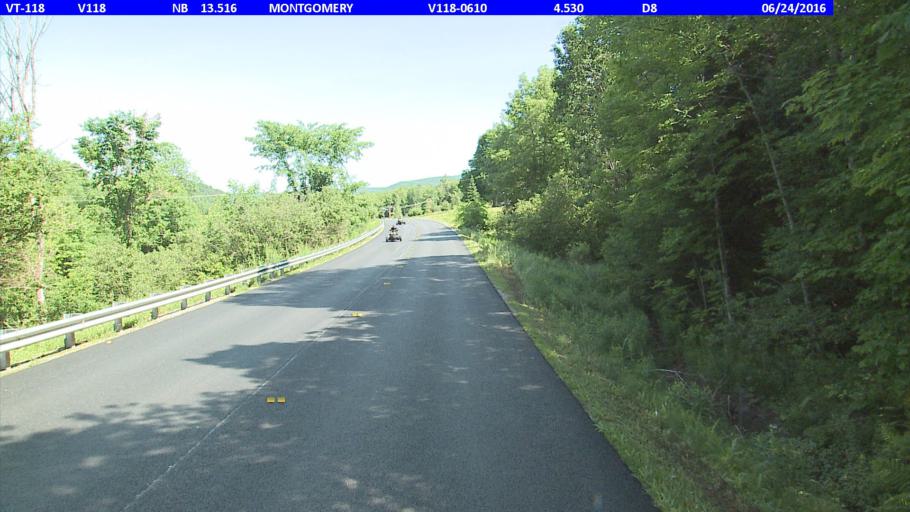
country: US
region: Vermont
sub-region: Franklin County
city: Richford
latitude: 44.8628
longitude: -72.6096
